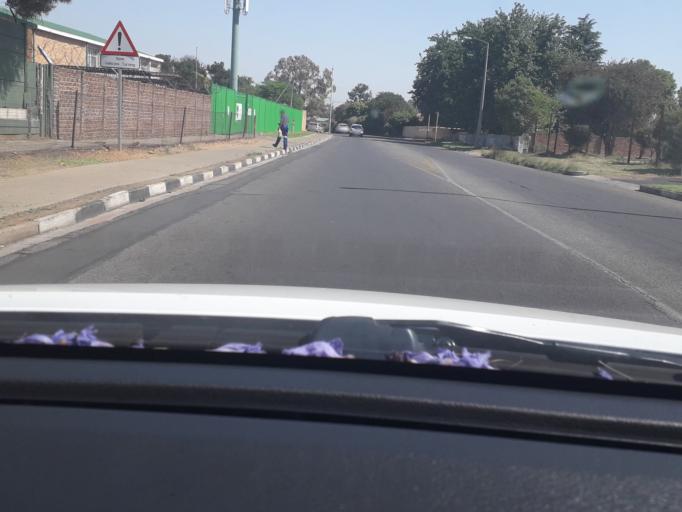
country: ZA
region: Gauteng
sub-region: Ekurhuleni Metropolitan Municipality
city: Benoni
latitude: -26.1869
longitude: 28.3023
